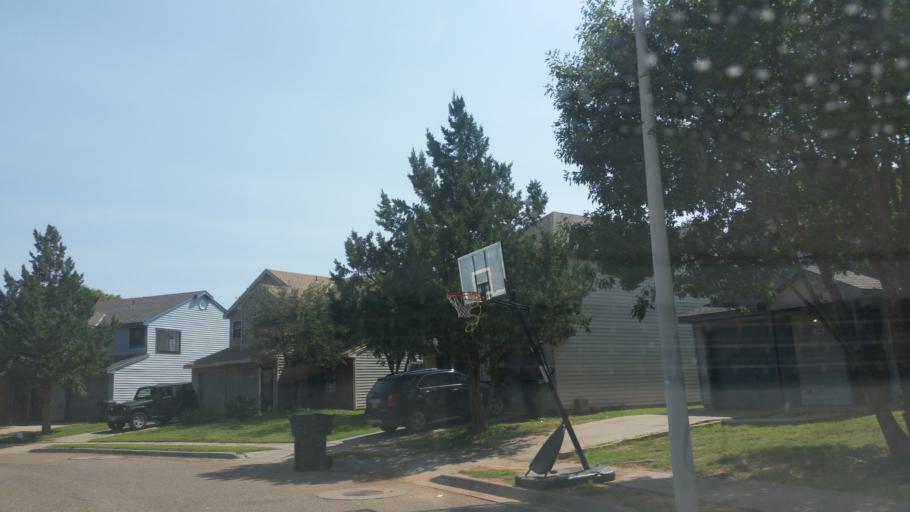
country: US
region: New Mexico
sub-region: Curry County
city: Clovis
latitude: 34.4468
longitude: -103.1753
